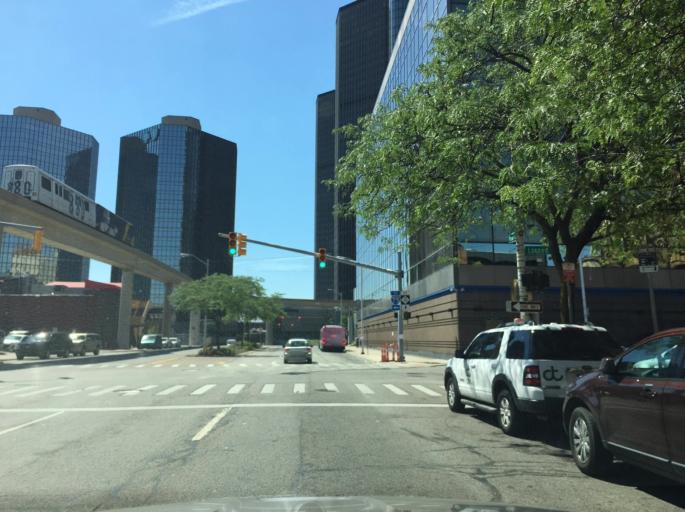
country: US
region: Michigan
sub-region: Wayne County
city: Detroit
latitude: 42.3318
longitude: -83.0405
